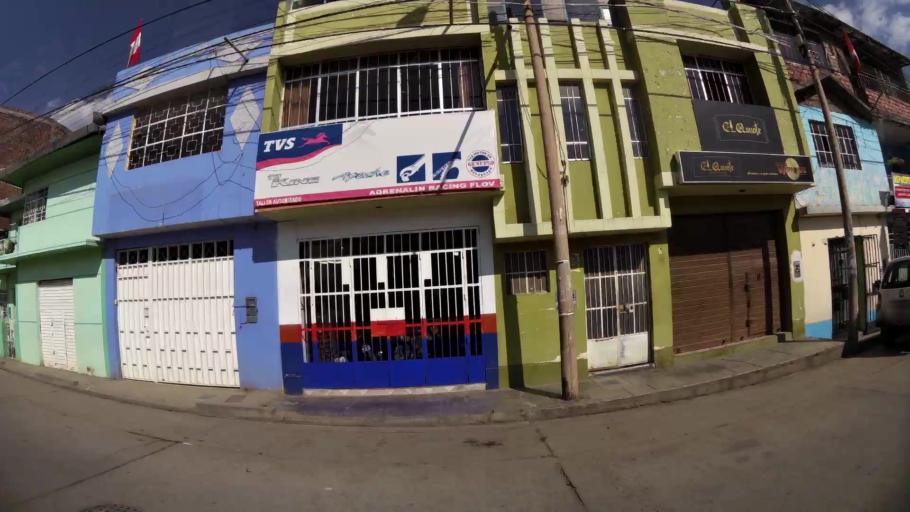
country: PE
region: Junin
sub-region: Provincia de Huancayo
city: El Tambo
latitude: -12.0641
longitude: -75.2170
